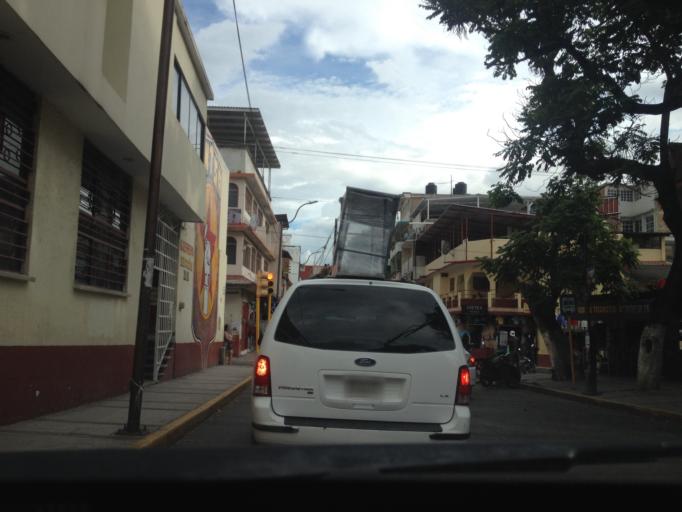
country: MX
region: Guerrero
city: Chilpancingo de los Bravos
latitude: 17.5549
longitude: -99.5039
